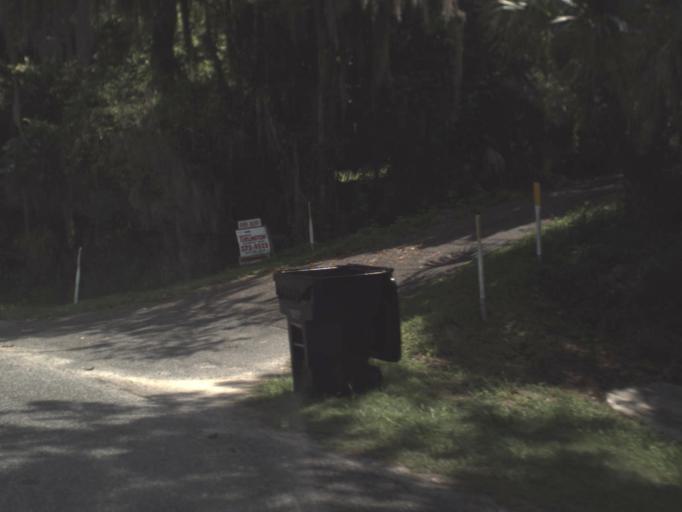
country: US
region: Florida
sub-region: Alachua County
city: Gainesville
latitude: 29.5319
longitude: -82.3088
